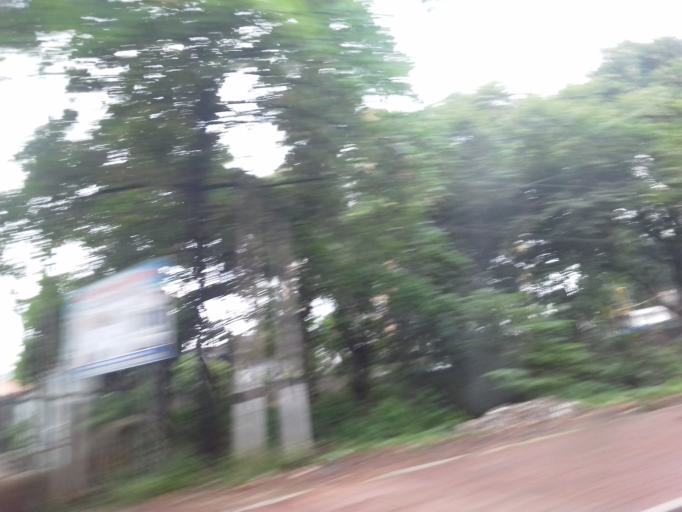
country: LK
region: Western
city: Battaramulla South
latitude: 6.9036
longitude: 79.9285
